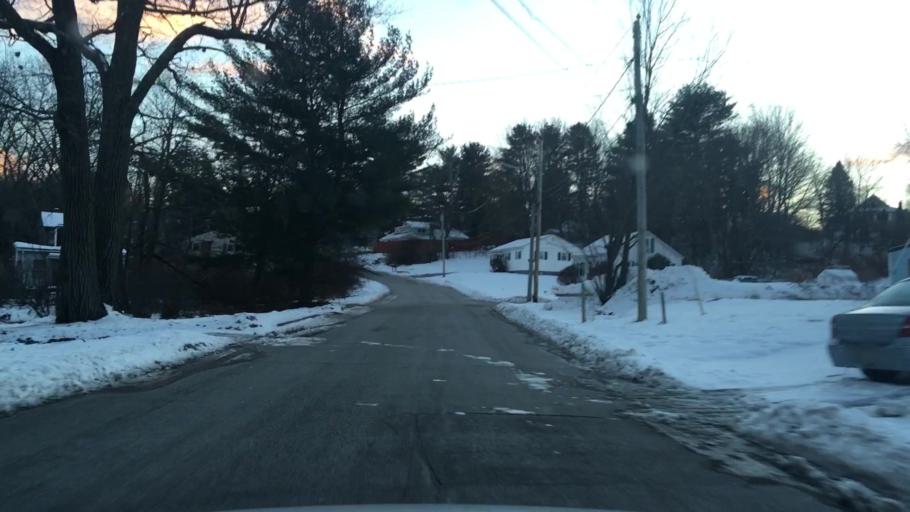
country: US
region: Maine
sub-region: Androscoggin County
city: Auburn
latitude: 44.0822
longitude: -70.2498
